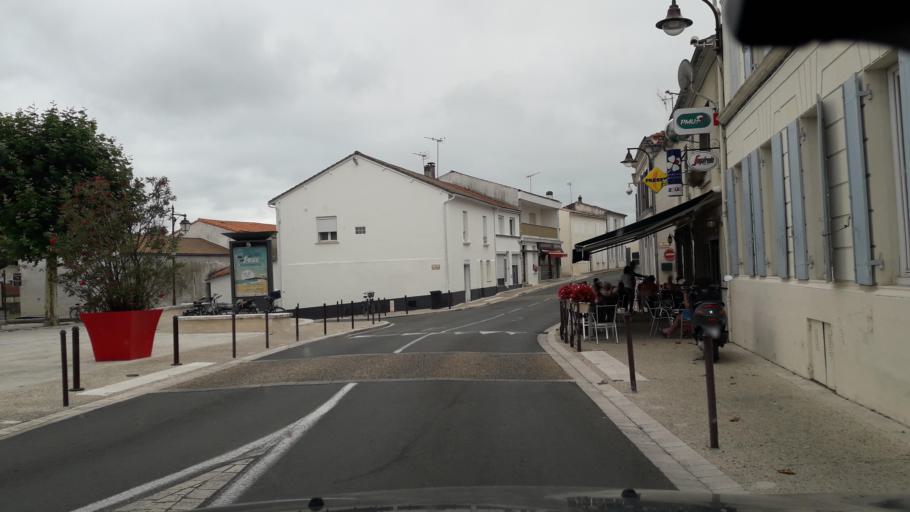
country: FR
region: Poitou-Charentes
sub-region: Departement de la Charente-Maritime
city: Les Mathes
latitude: 45.7172
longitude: -1.1473
